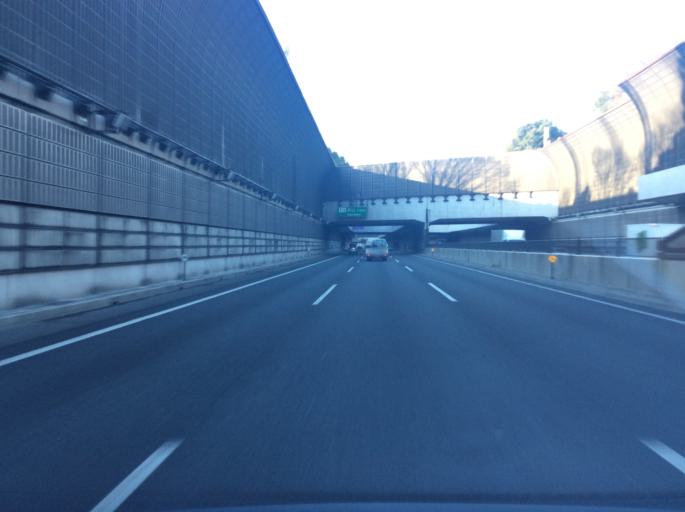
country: JP
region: Chiba
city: Nagareyama
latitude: 35.8909
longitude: 139.9154
